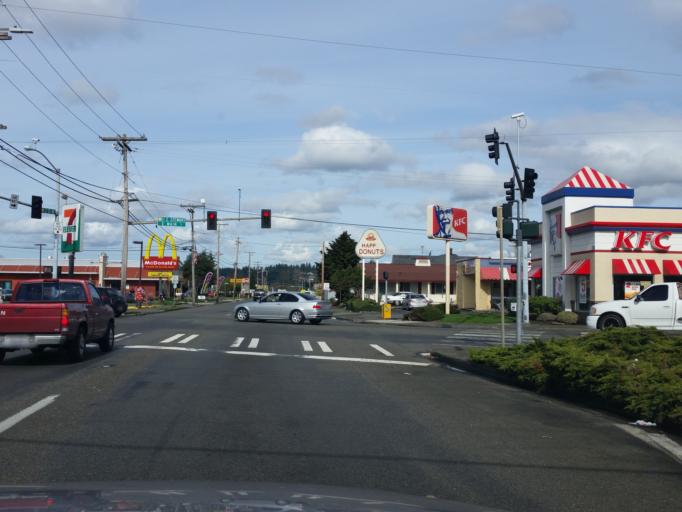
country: US
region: Washington
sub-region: Pierce County
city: Puyallup
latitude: 47.1926
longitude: -122.2921
